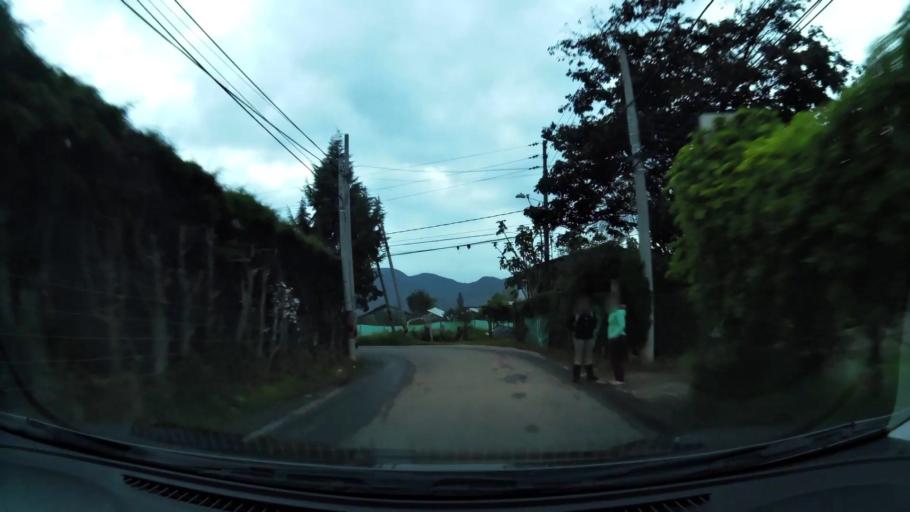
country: CO
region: Cundinamarca
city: Chia
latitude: 4.8412
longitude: -74.0655
